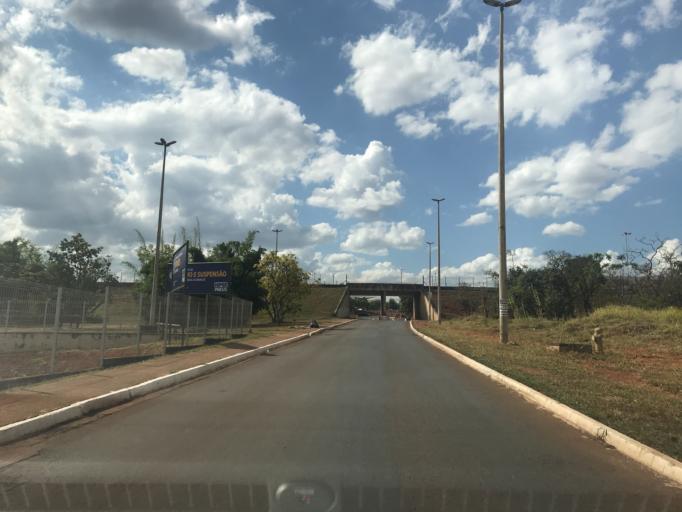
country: BR
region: Federal District
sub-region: Brasilia
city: Brasilia
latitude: -15.8337
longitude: -47.9494
